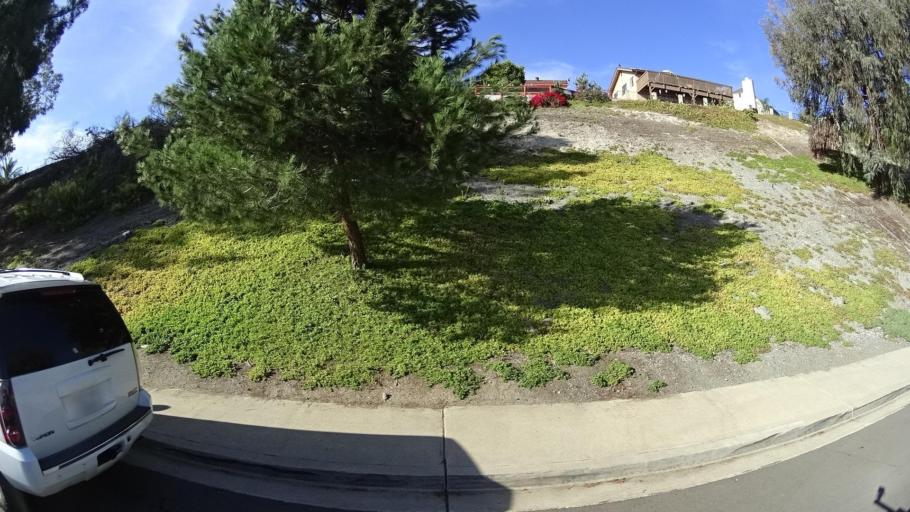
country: US
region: California
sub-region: San Diego County
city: Rancho San Diego
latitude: 32.7387
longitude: -116.9593
